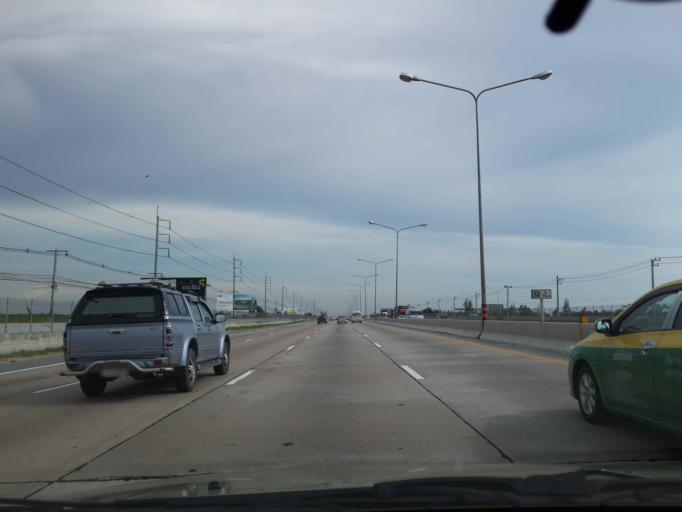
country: TH
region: Chon Buri
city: Si Racha
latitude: 13.1642
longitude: 100.9900
